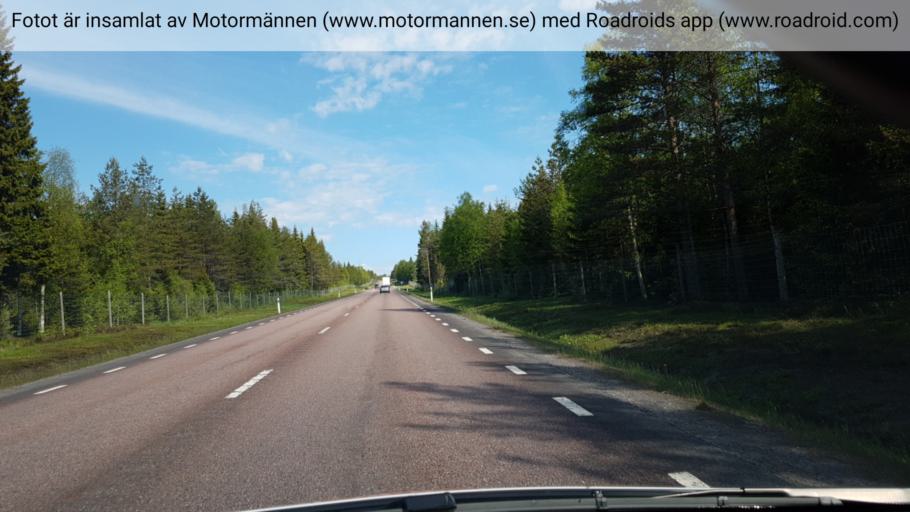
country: SE
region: Vaesterbotten
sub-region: Skelleftea Kommun
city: Burea
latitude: 64.4223
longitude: 21.2860
